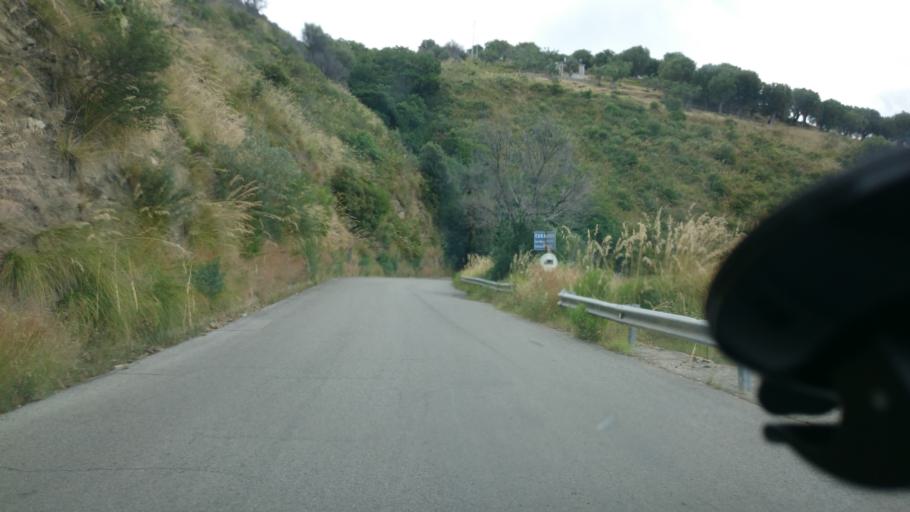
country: IT
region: Campania
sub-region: Provincia di Salerno
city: Pisciotta
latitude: 40.1115
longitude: 15.2256
